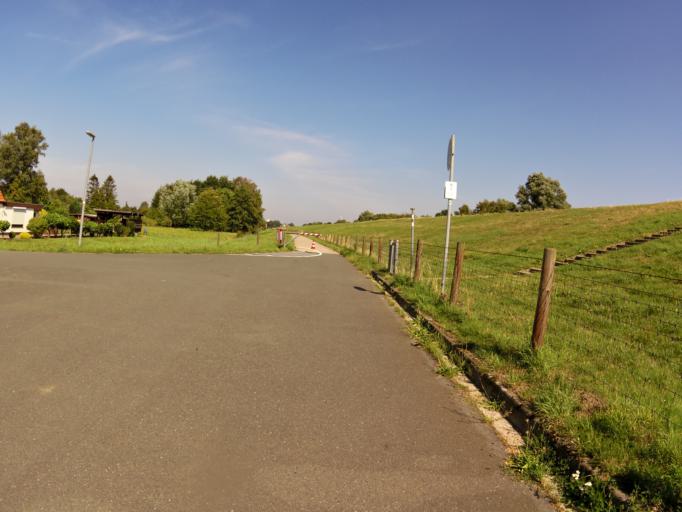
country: DE
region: Lower Saxony
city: Brake (Unterweser)
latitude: 53.2951
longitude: 8.4854
